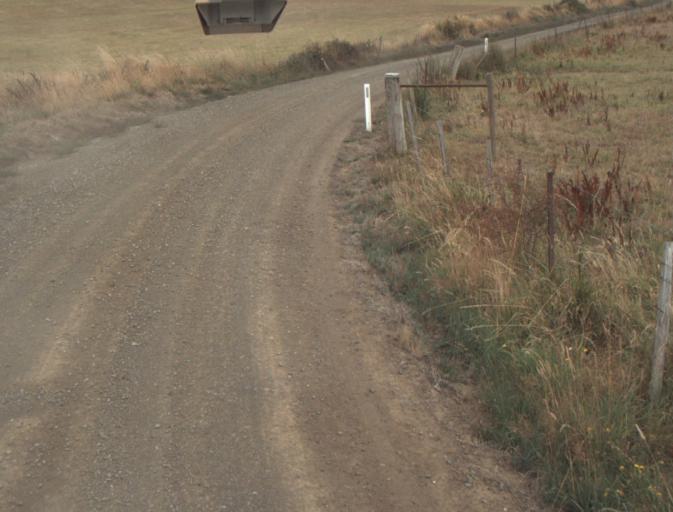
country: AU
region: Tasmania
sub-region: Launceston
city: Mayfield
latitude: -41.2134
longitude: 147.1479
